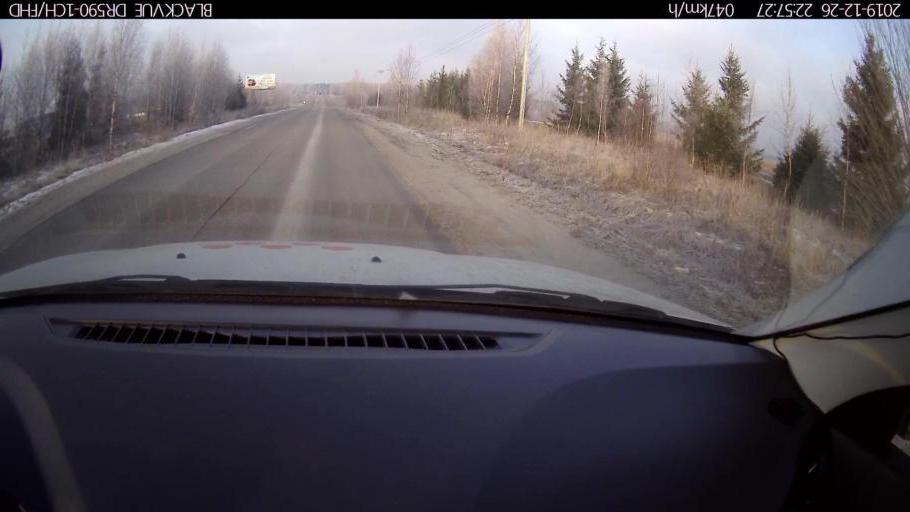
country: RU
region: Nizjnij Novgorod
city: Burevestnik
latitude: 56.1509
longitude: 43.7157
